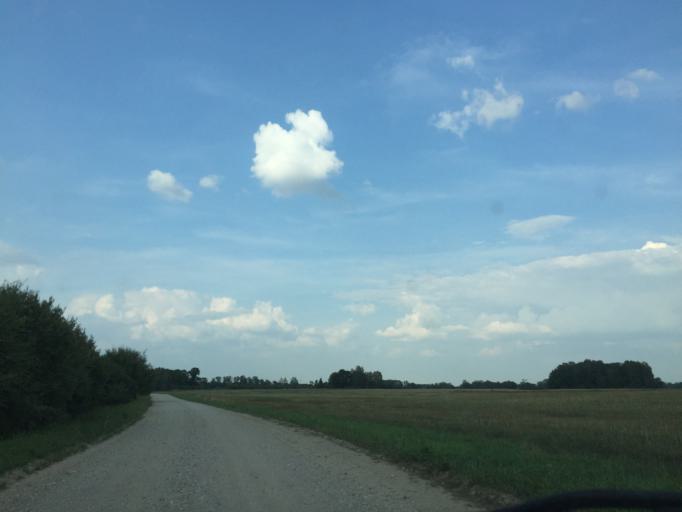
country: LT
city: Zagare
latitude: 56.4794
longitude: 23.1474
